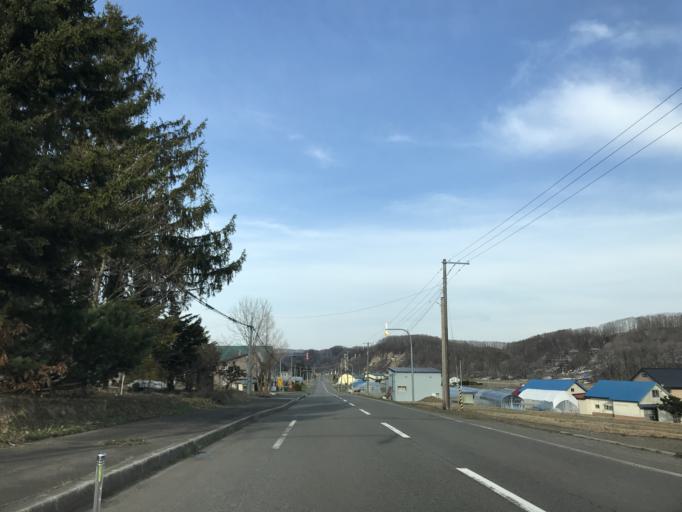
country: JP
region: Hokkaido
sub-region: Asahikawa-shi
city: Asahikawa
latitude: 43.6974
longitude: 142.3358
